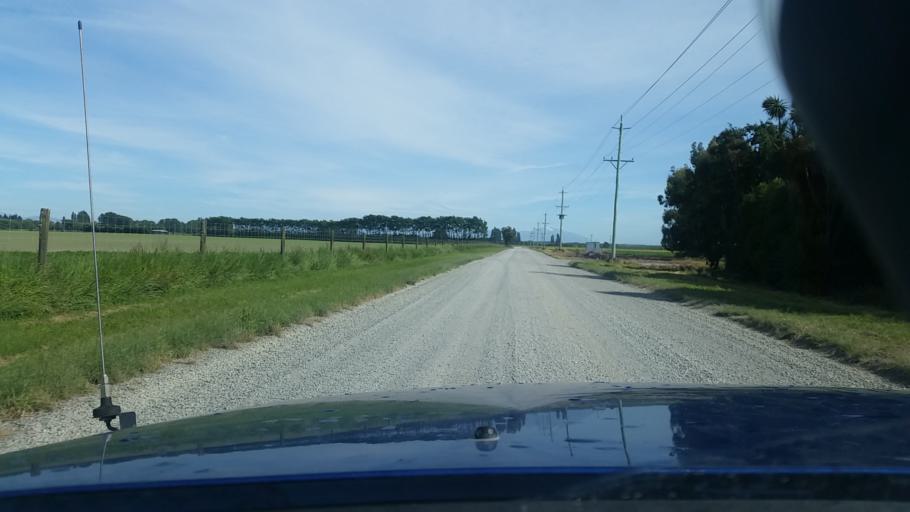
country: NZ
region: Canterbury
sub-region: Ashburton District
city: Tinwald
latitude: -43.9833
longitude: 171.7874
